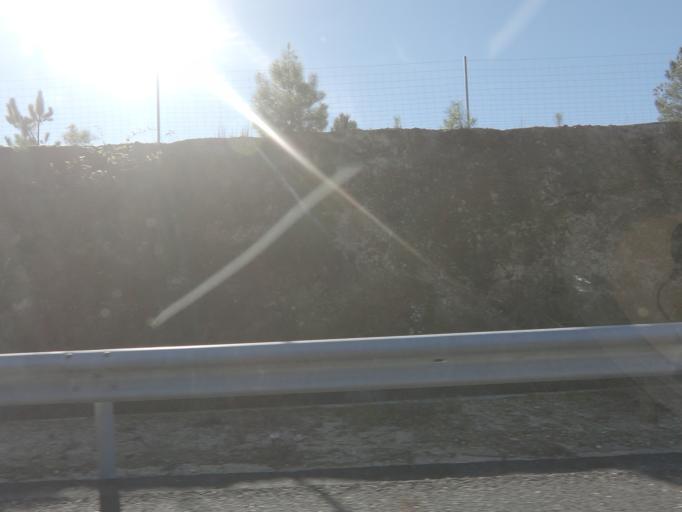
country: ES
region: Galicia
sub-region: Provincia de Ourense
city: Pinor
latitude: 42.5241
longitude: -8.0119
